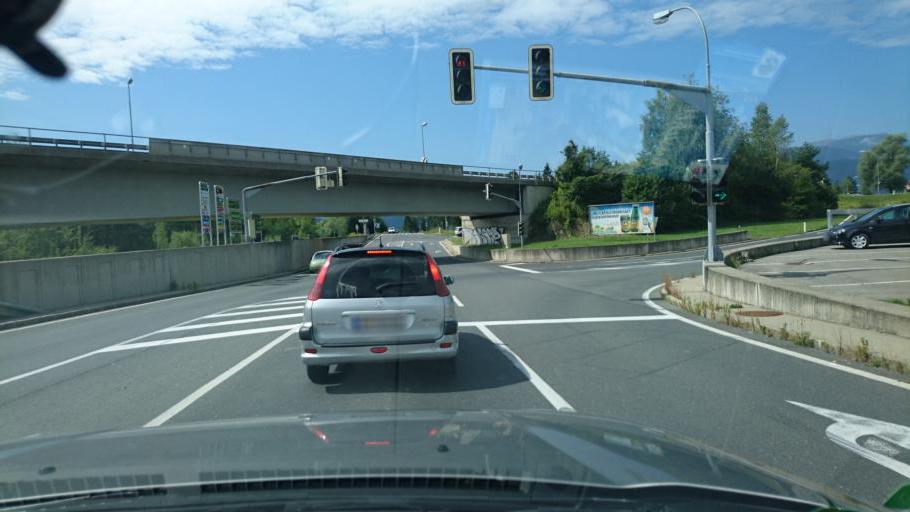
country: AT
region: Carinthia
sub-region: Villach Stadt
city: Villach
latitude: 46.6039
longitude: 13.8751
